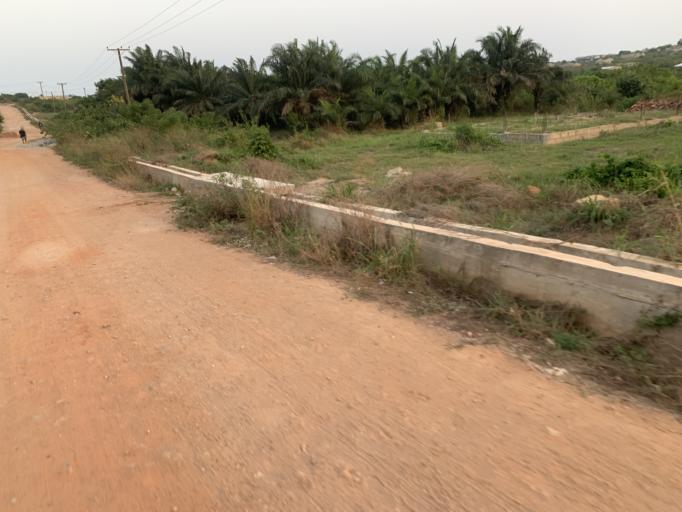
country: GH
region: Central
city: Winneba
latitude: 5.3766
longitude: -0.6102
